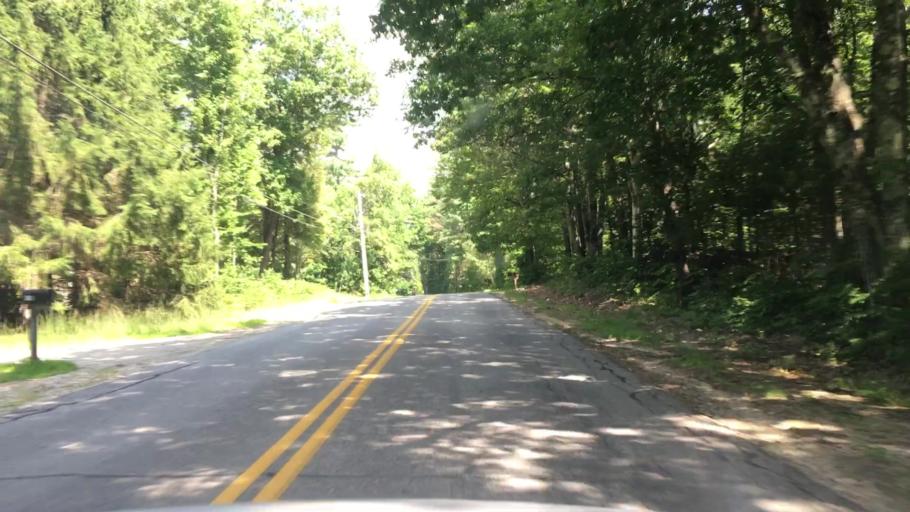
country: US
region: Maine
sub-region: Cumberland County
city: Raymond
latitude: 43.9454
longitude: -70.5257
